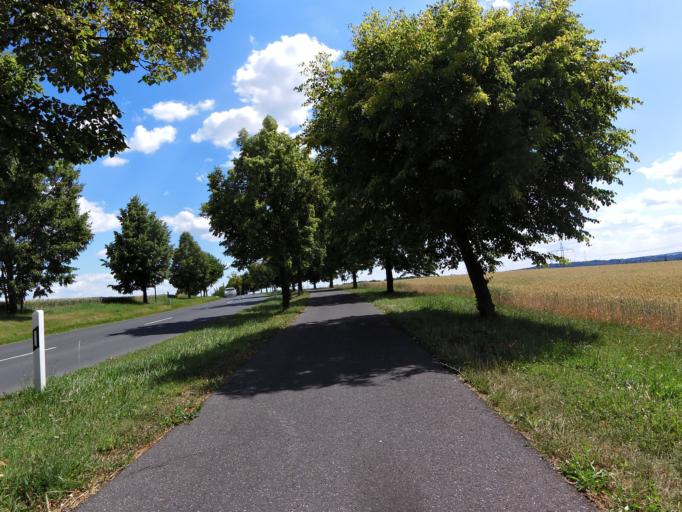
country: DE
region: Bavaria
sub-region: Regierungsbezirk Unterfranken
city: Wuerzburg
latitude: 49.8185
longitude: 9.9316
